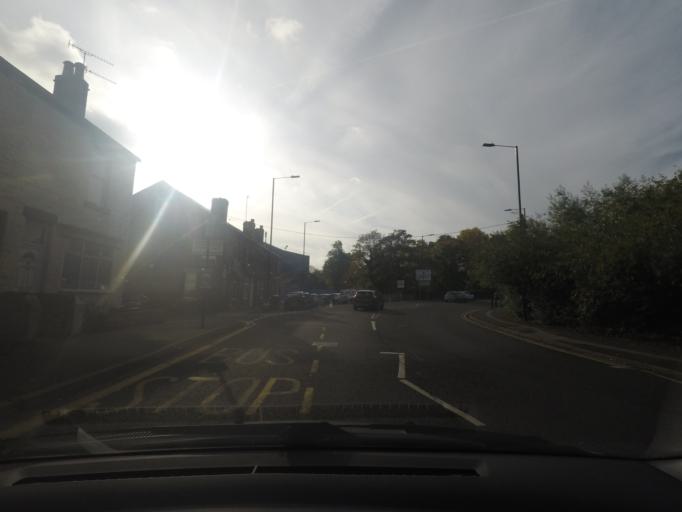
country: GB
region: England
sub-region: Sheffield
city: Oughtibridge
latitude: 53.4125
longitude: -1.5027
